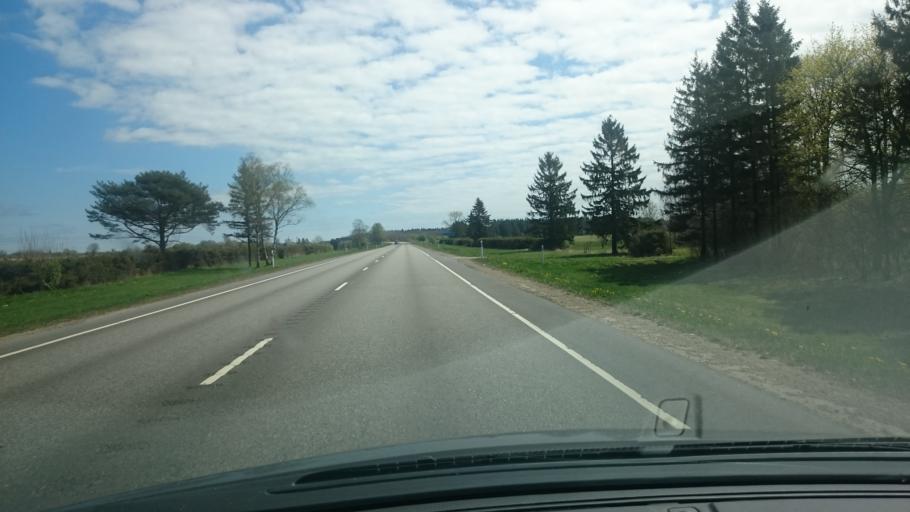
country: EE
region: Ida-Virumaa
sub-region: Kohtla-Nomme vald
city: Kohtla-Nomme
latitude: 59.4217
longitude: 27.1910
